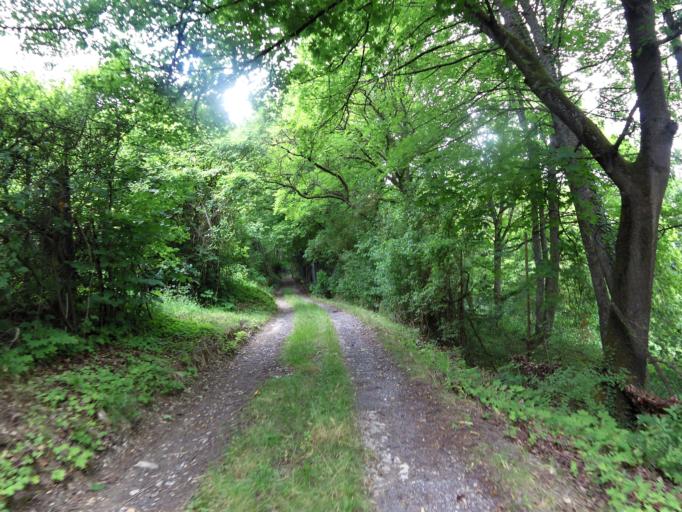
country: DE
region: Bavaria
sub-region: Regierungsbezirk Unterfranken
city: Wuerzburg
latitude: 49.7679
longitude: 9.9282
